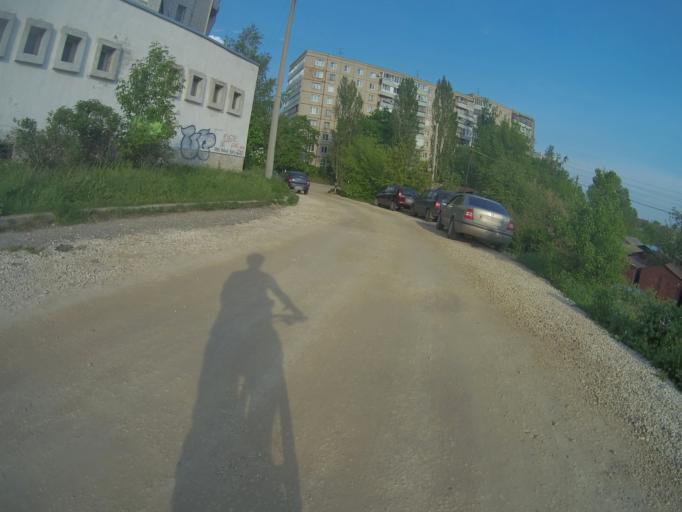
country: RU
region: Vladimir
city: Vladimir
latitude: 56.1664
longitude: 40.4401
